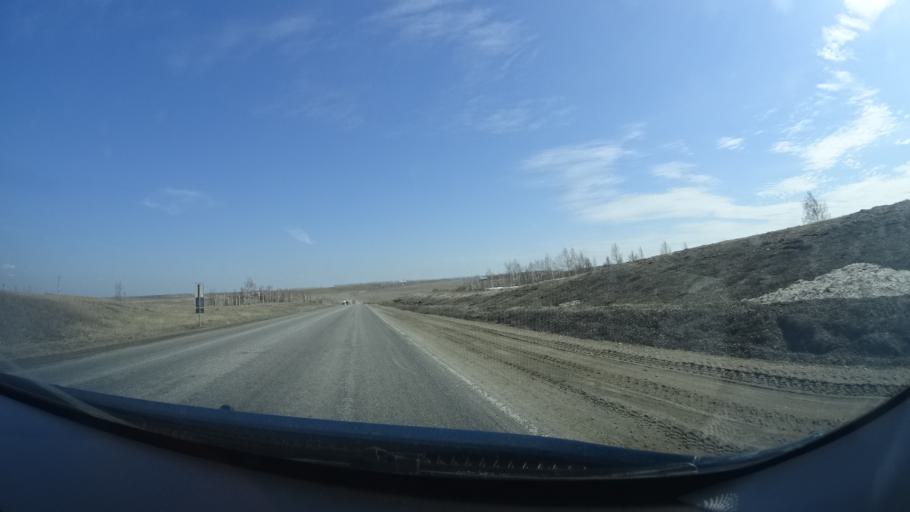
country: RU
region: Bashkortostan
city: Serafimovskiy
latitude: 54.4562
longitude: 53.6974
